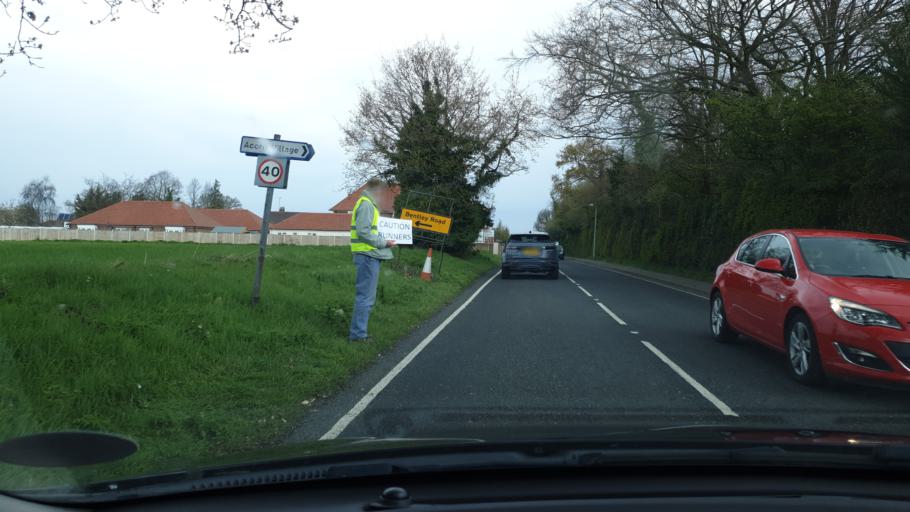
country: GB
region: England
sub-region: Essex
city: Manningtree
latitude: 51.9380
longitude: 1.0626
